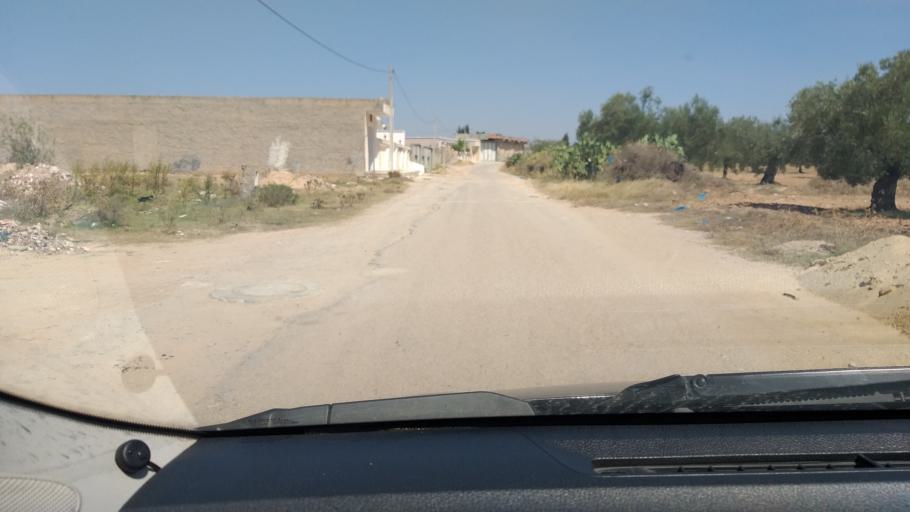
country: TN
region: Al Mahdiyah
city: El Jem
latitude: 35.2892
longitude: 10.7206
